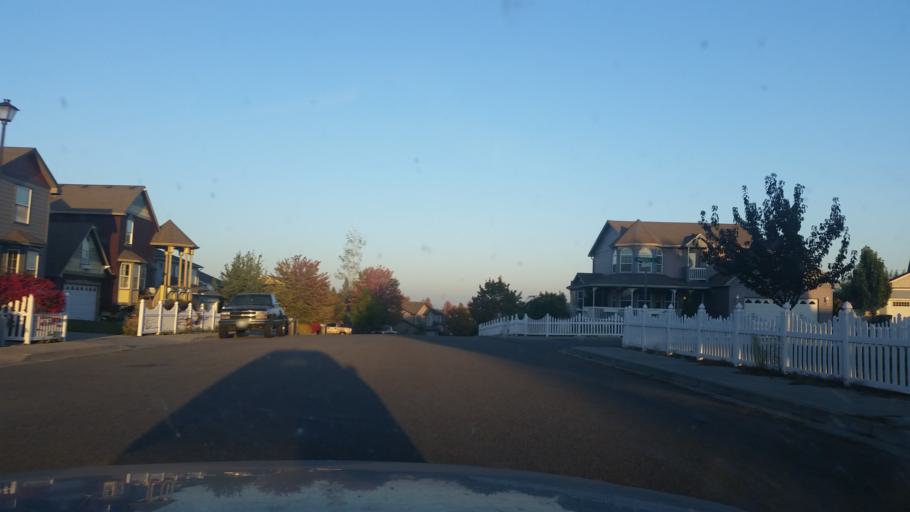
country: US
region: Washington
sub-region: Spokane County
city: Cheney
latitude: 47.5015
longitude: -117.5793
